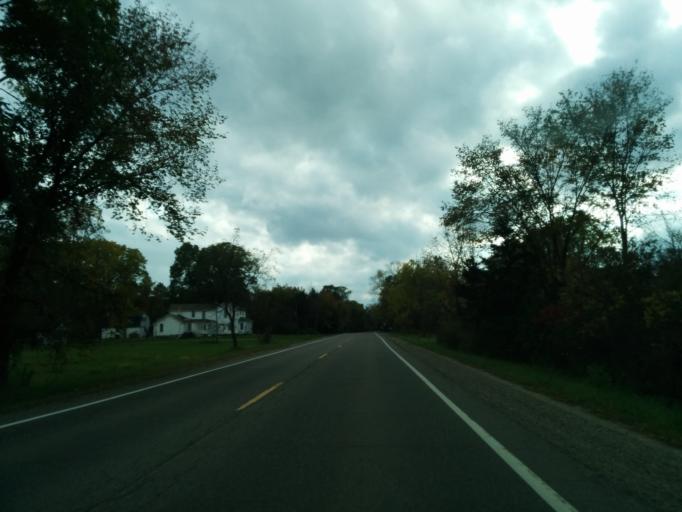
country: US
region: Michigan
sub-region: Oakland County
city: Waterford
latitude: 42.6621
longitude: -83.4908
